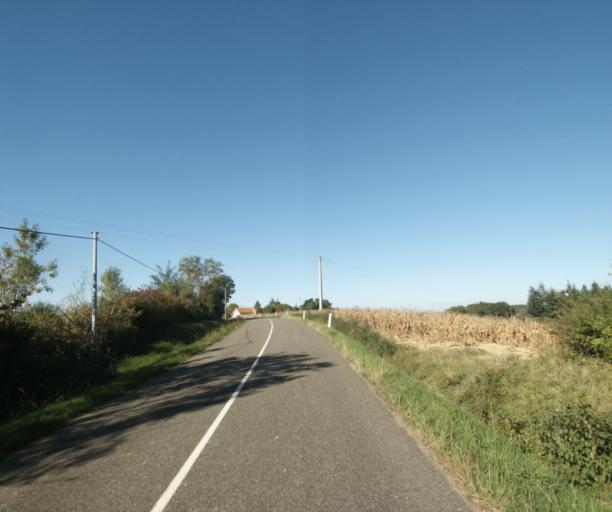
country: FR
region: Midi-Pyrenees
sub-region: Departement du Gers
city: Eauze
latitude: 43.8178
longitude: 0.1686
